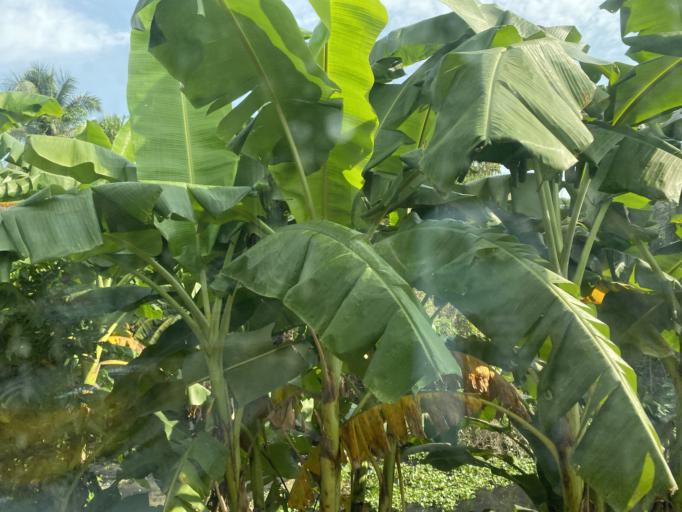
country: BD
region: Dhaka
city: Bhairab Bazar
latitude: 23.9666
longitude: 91.1161
